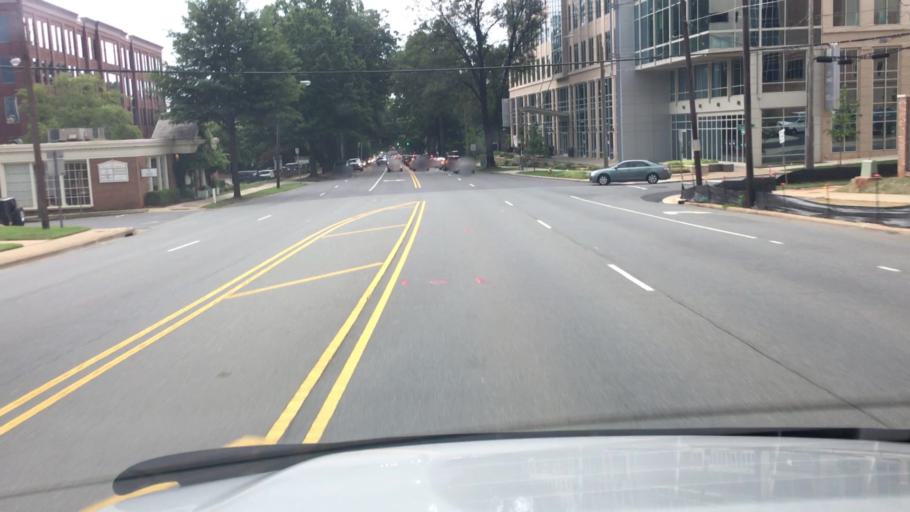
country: US
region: North Carolina
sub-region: Mecklenburg County
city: Charlotte
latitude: 35.2178
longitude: -80.8482
